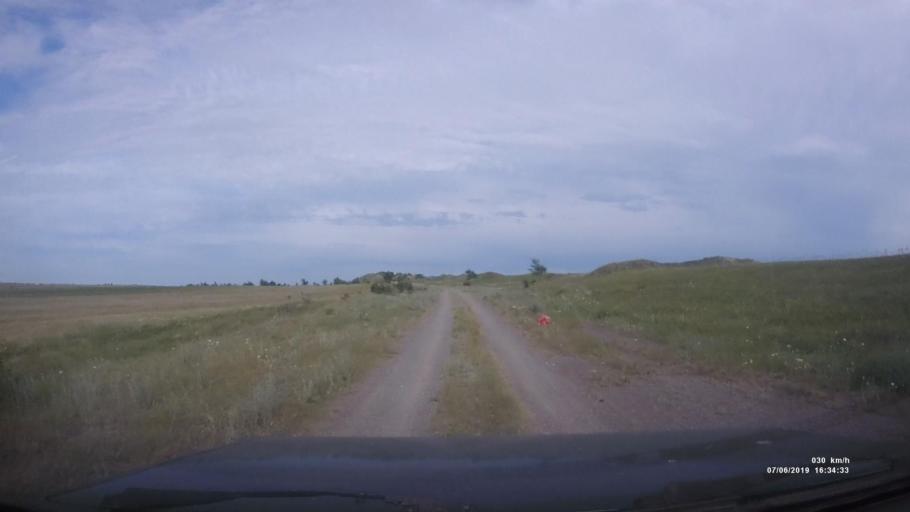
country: RU
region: Rostov
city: Staraya Stanitsa
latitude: 48.2512
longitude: 40.3422
